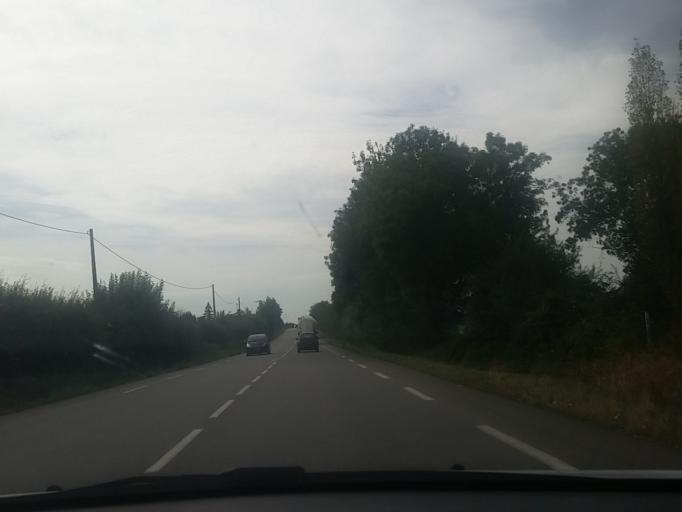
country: FR
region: Pays de la Loire
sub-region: Departement de la Vendee
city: Sainte-Cecile
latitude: 46.7247
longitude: -1.0755
